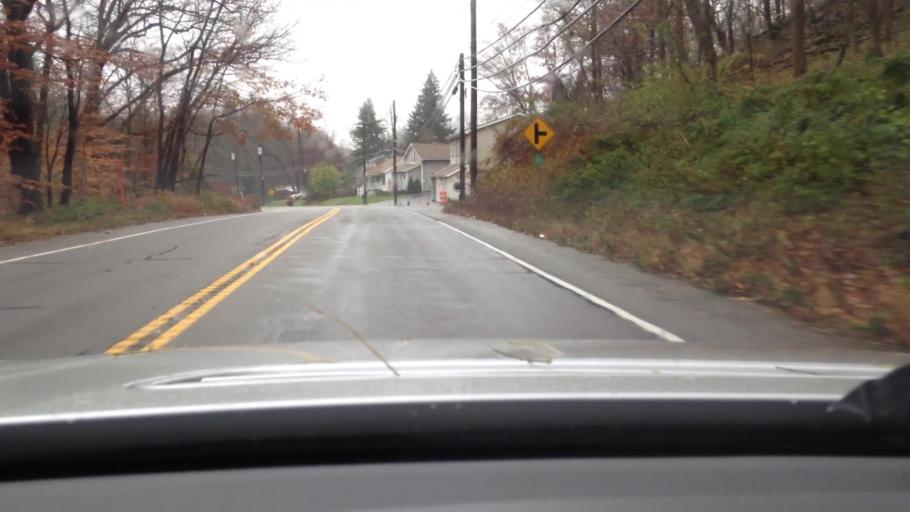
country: US
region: New York
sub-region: Westchester County
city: Peekskill
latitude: 41.3203
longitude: -73.9299
